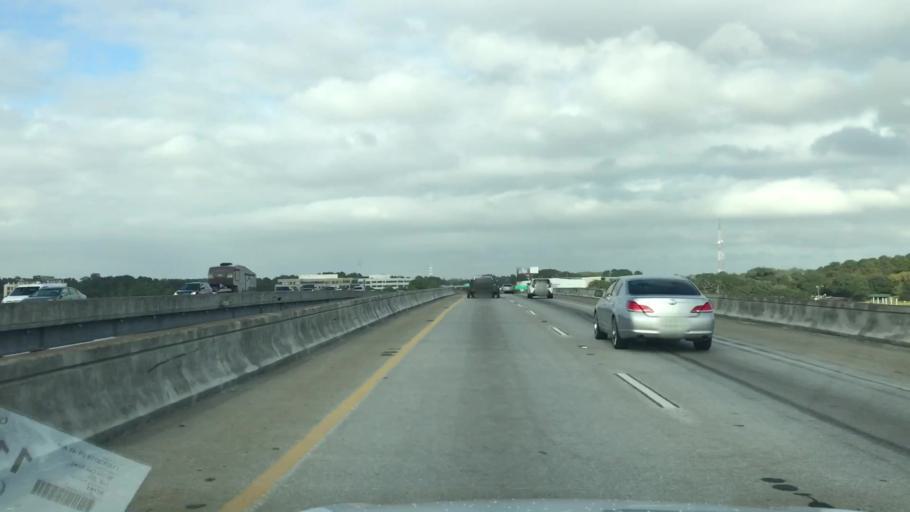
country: US
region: South Carolina
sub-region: Charleston County
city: North Charleston
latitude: 32.8342
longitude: -80.0255
